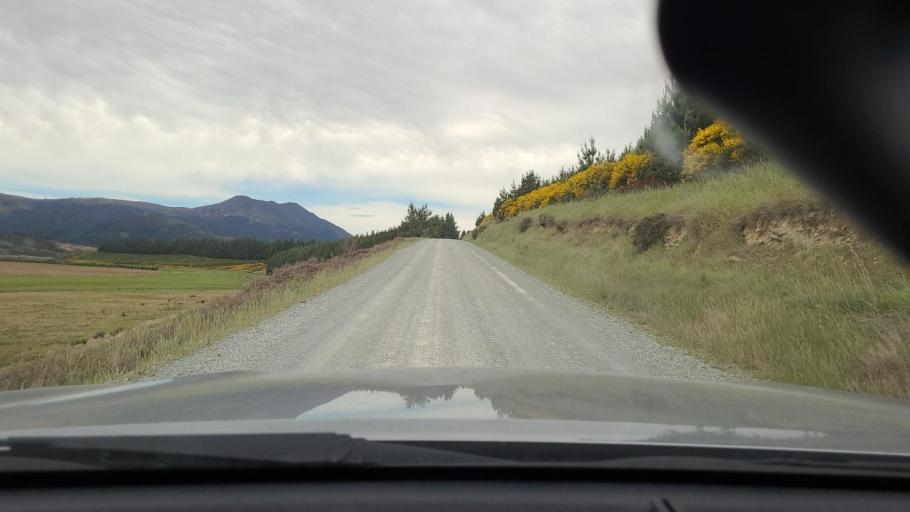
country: NZ
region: Southland
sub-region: Southland District
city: Te Anau
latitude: -45.5252
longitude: 168.1186
